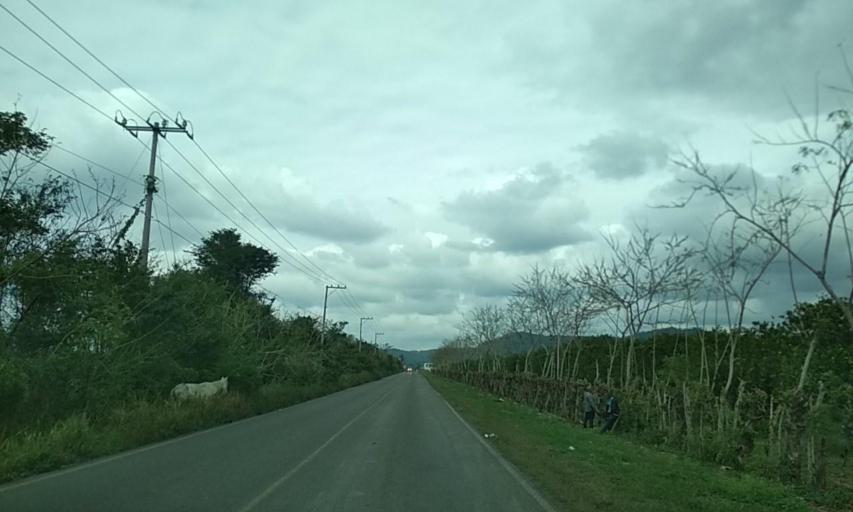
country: MX
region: Veracruz
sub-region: Papantla
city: El Chote
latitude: 20.3866
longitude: -97.3366
